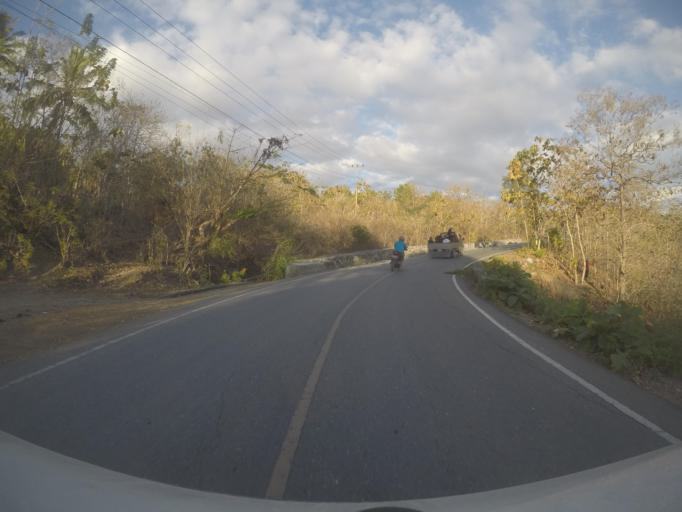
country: TL
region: Bobonaro
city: Maliana
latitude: -8.9623
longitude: 125.0344
